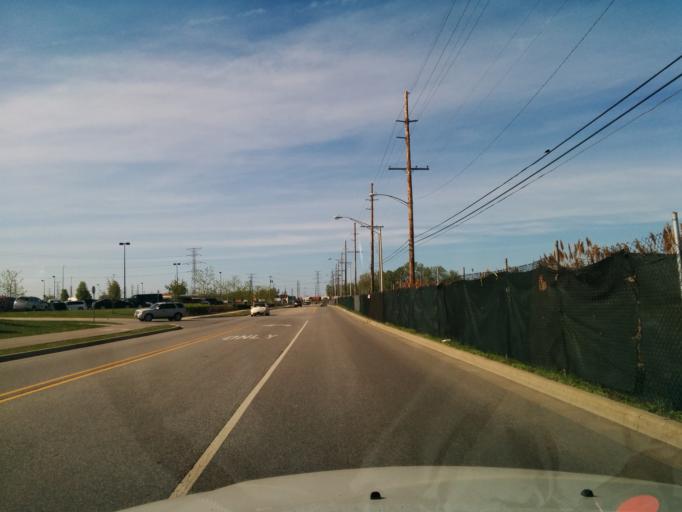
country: US
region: Indiana
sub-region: Lake County
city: Whiting
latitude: 41.6928
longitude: -87.5181
